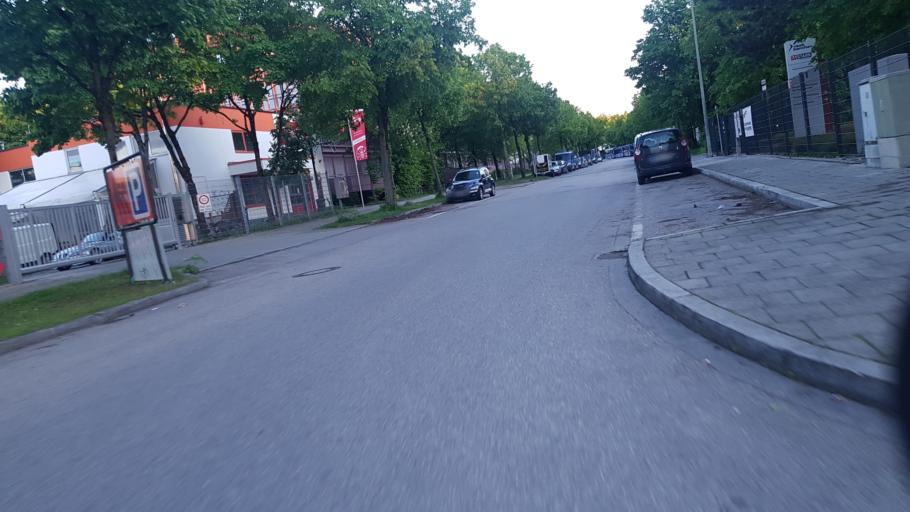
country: DE
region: Bavaria
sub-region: Upper Bavaria
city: Bogenhausen
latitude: 48.1373
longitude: 11.6637
